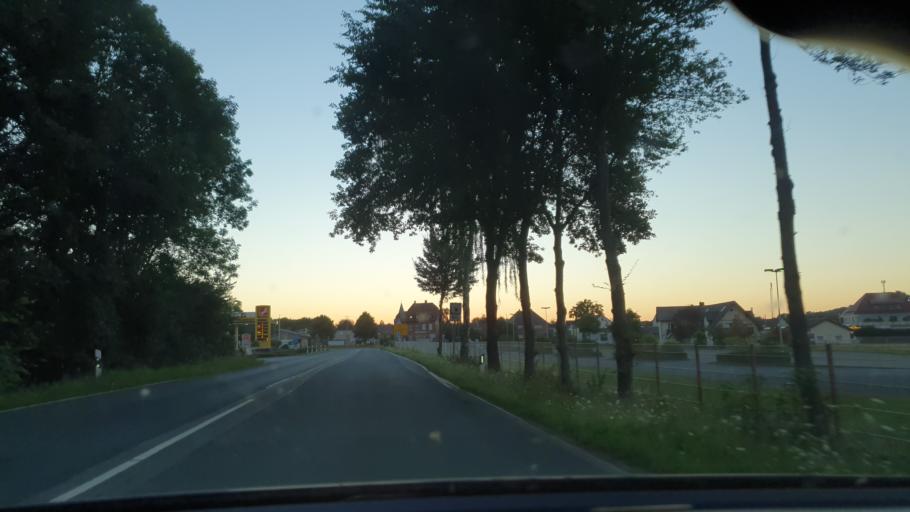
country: DE
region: North Rhine-Westphalia
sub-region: Regierungsbezirk Detmold
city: Rodinghausen
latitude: 52.1998
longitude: 8.4588
